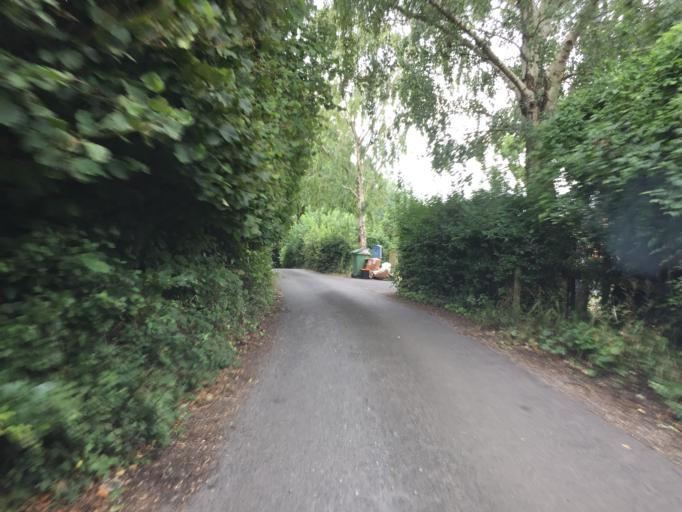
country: GB
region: England
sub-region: Kent
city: Maidstone
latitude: 51.2377
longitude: 0.5404
